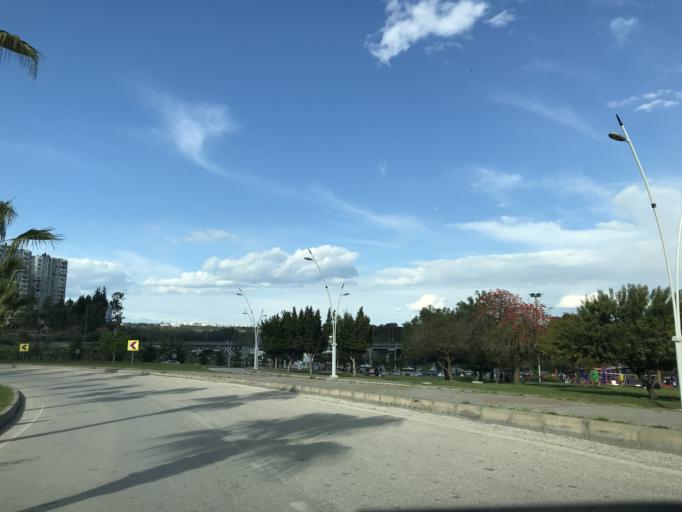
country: TR
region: Adana
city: Adana
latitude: 37.0225
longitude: 35.3205
